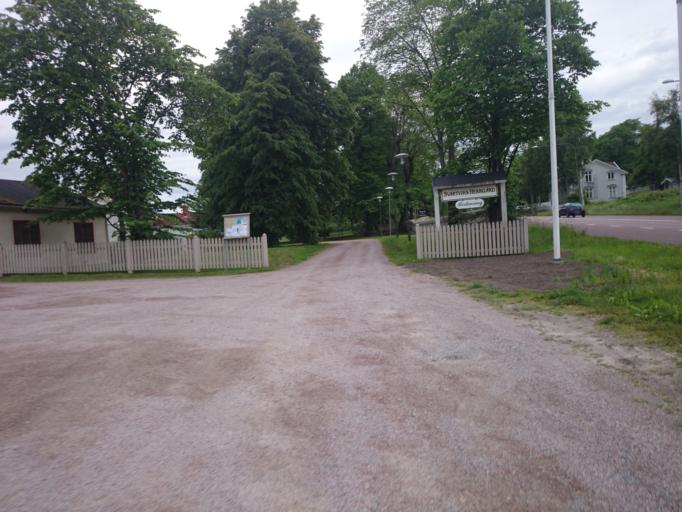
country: SE
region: Vaesternorrland
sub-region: Sundsvalls Kommun
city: Stockvik
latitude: 62.3172
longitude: 17.3699
